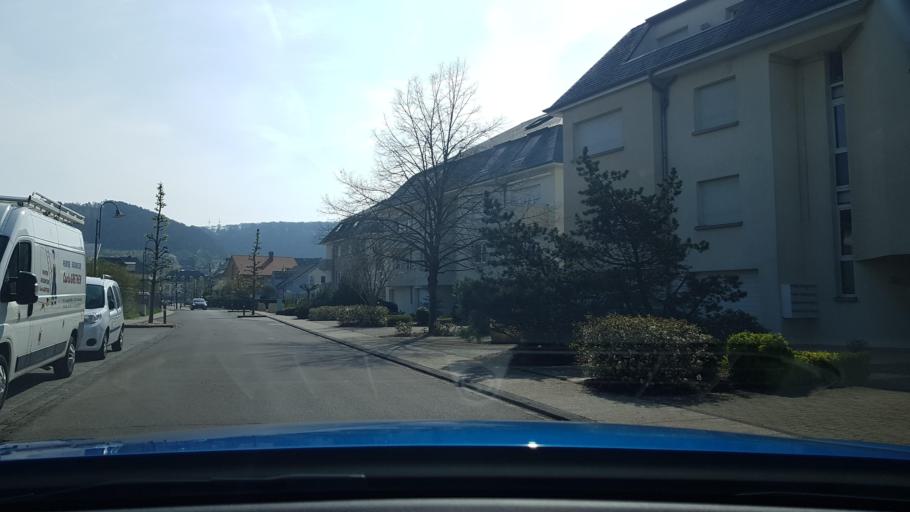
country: LU
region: Luxembourg
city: Bereldange
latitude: 49.6633
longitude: 6.1291
